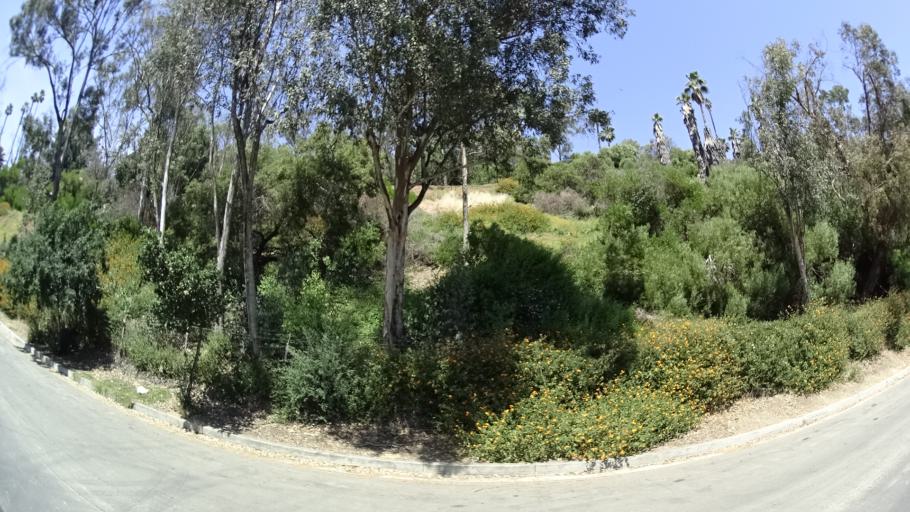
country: US
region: California
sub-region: Los Angeles County
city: Echo Park
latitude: 34.0711
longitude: -118.2446
